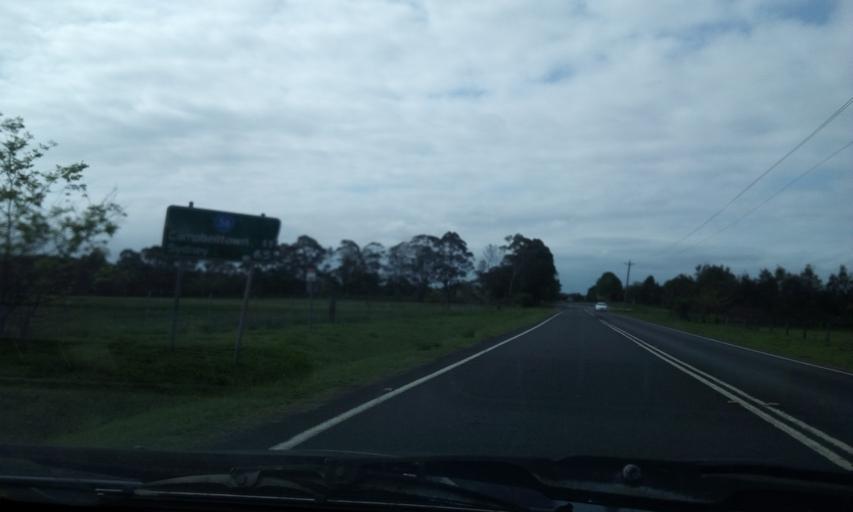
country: AU
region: New South Wales
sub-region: Campbelltown Municipality
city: Glen Alpine
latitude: -34.1222
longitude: 150.7390
